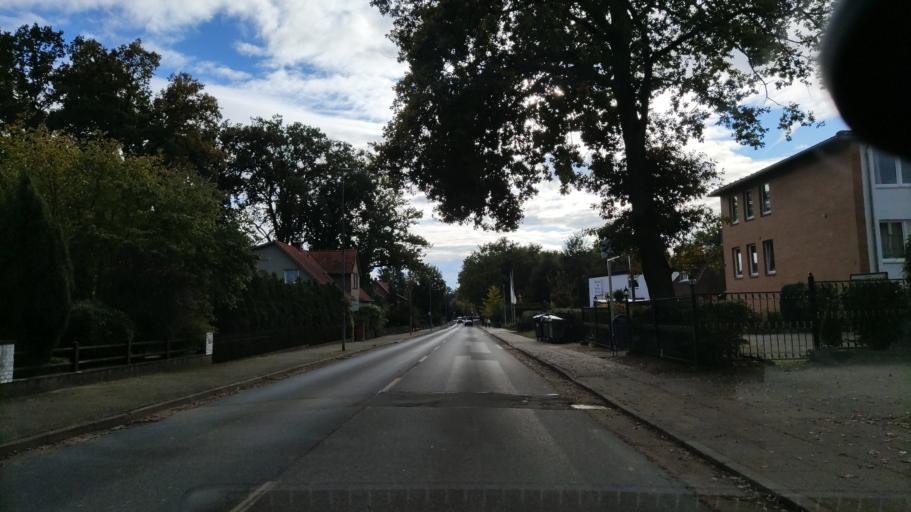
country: DE
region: Lower Saxony
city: Bad Bevensen
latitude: 53.0821
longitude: 10.5921
